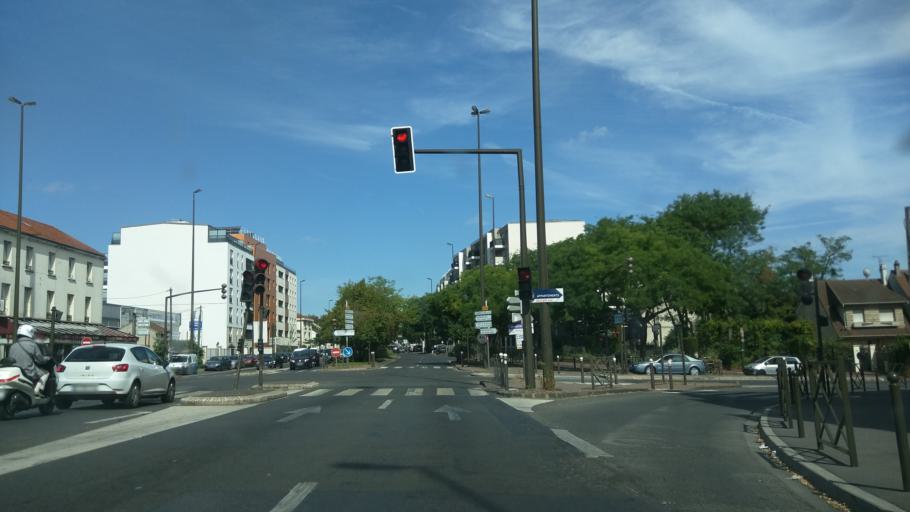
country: FR
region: Ile-de-France
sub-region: Departement des Yvelines
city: Sartrouville
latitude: 48.9410
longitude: 2.2070
